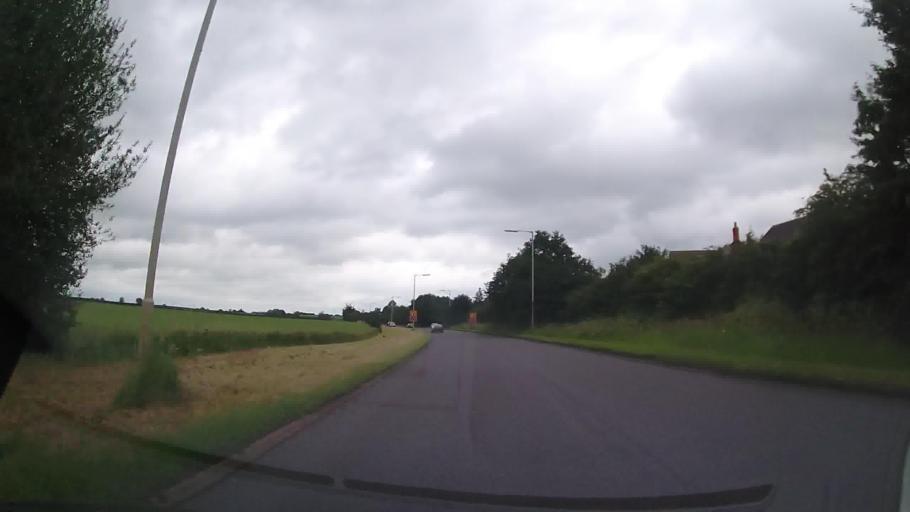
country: GB
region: England
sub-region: Shropshire
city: Market Drayton
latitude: 52.9039
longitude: -2.5057
